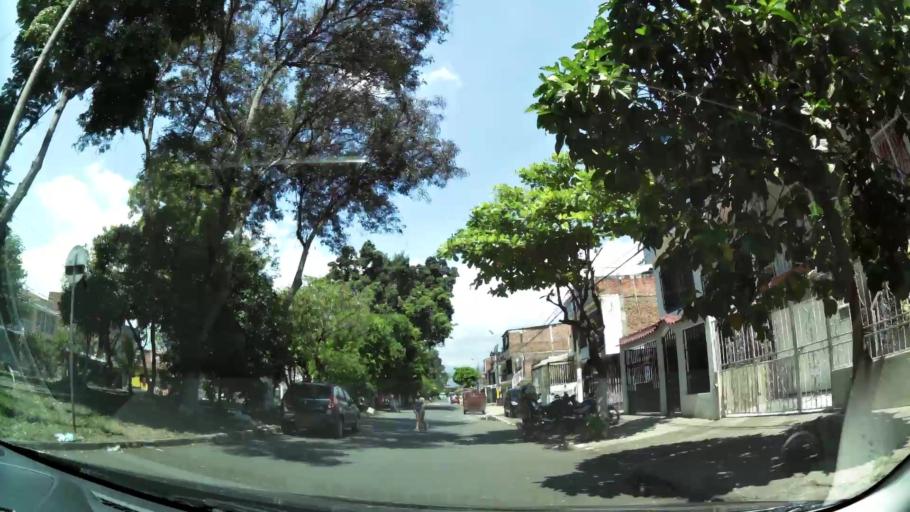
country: CO
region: Valle del Cauca
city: Cali
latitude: 3.4351
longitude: -76.4978
